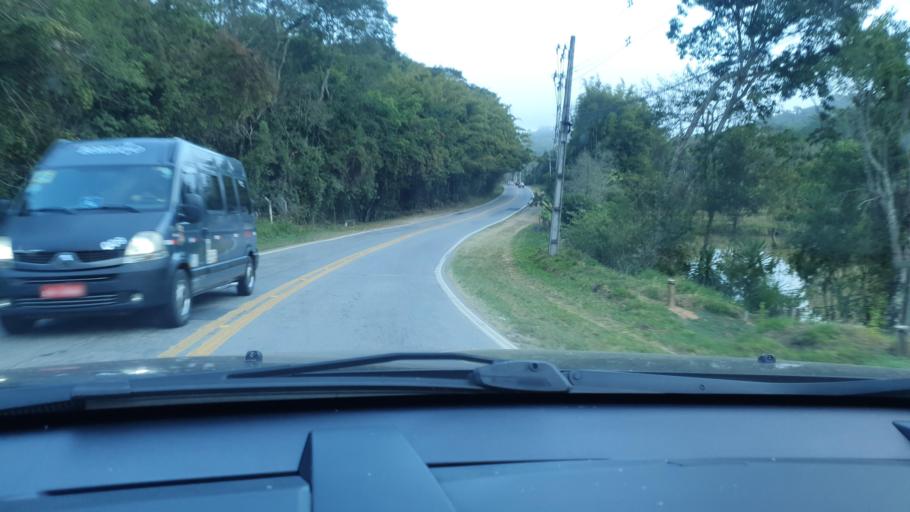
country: BR
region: Sao Paulo
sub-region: Ibiuna
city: Ibiuna
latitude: -23.6837
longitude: -47.2760
